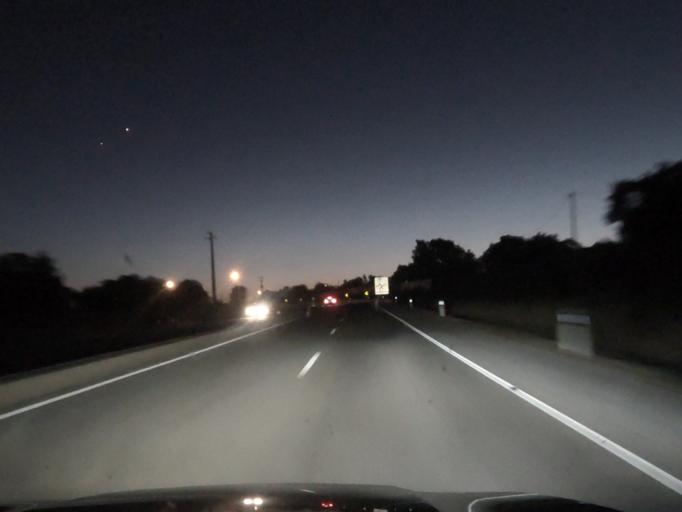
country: PT
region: Faro
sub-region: Loule
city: Loule
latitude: 37.1454
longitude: -8.0384
